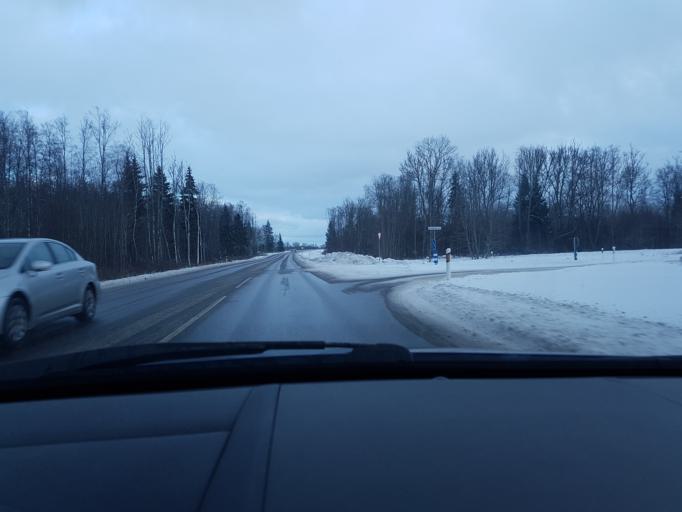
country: EE
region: Harju
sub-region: Kiili vald
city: Kiili
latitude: 59.3464
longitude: 24.8065
